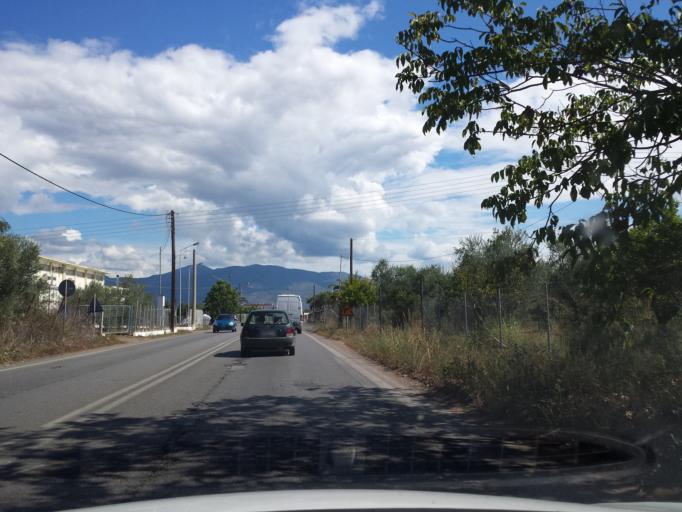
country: GR
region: Peloponnese
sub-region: Nomos Messinias
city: Messini
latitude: 37.0390
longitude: 21.9920
